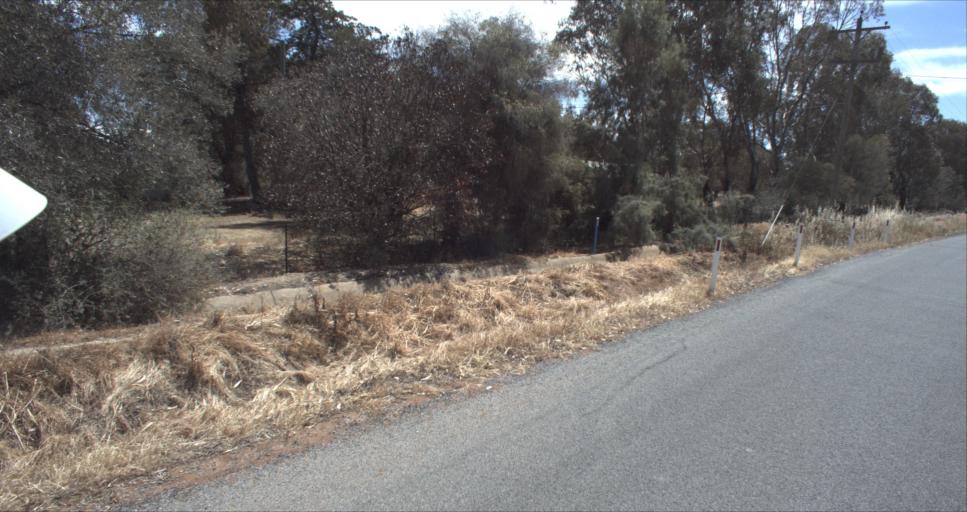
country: AU
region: New South Wales
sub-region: Leeton
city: Leeton
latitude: -34.5816
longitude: 146.4275
